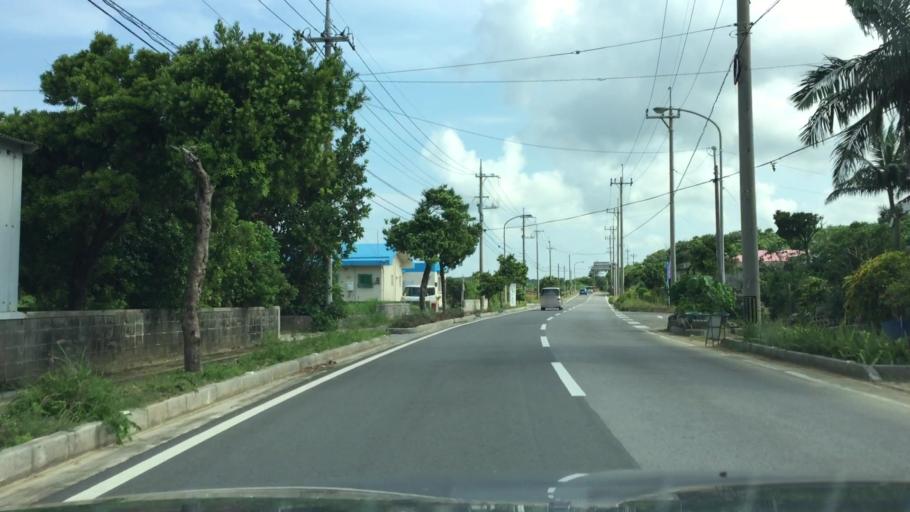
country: JP
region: Okinawa
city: Ishigaki
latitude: 24.4629
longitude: 124.2504
